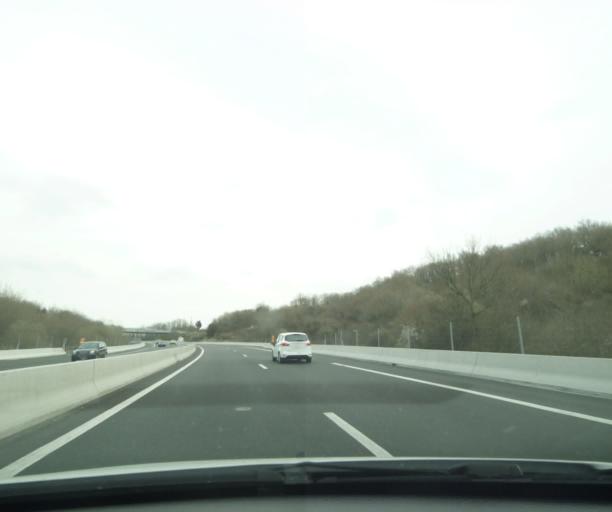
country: FR
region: Aquitaine
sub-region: Departement des Pyrenees-Atlantiques
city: Mouguerre
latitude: 43.4578
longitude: -1.4187
